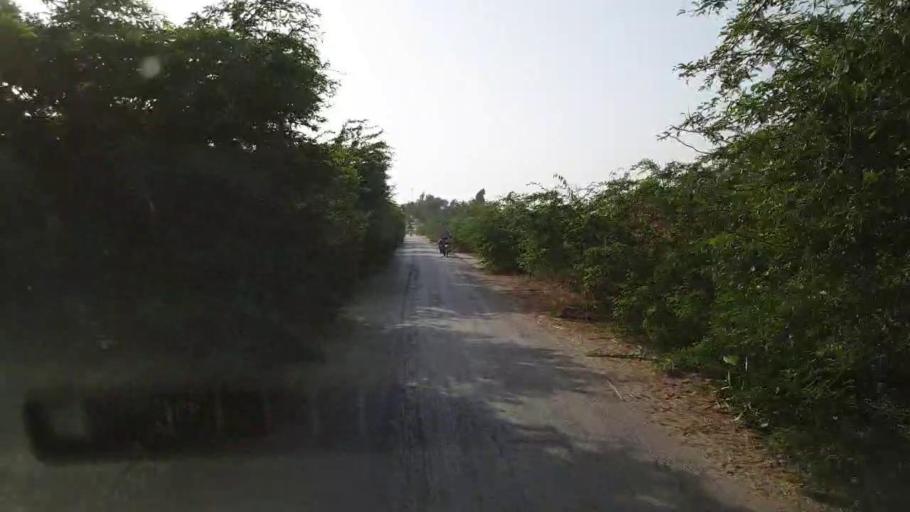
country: PK
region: Sindh
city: Jam Sahib
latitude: 26.4333
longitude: 68.8759
